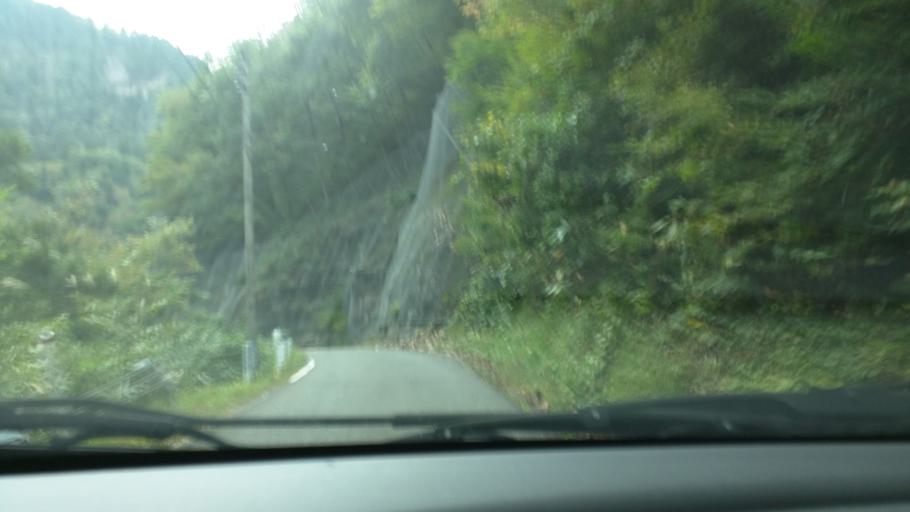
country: JP
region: Fukushima
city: Kitakata
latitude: 37.4575
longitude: 139.6975
